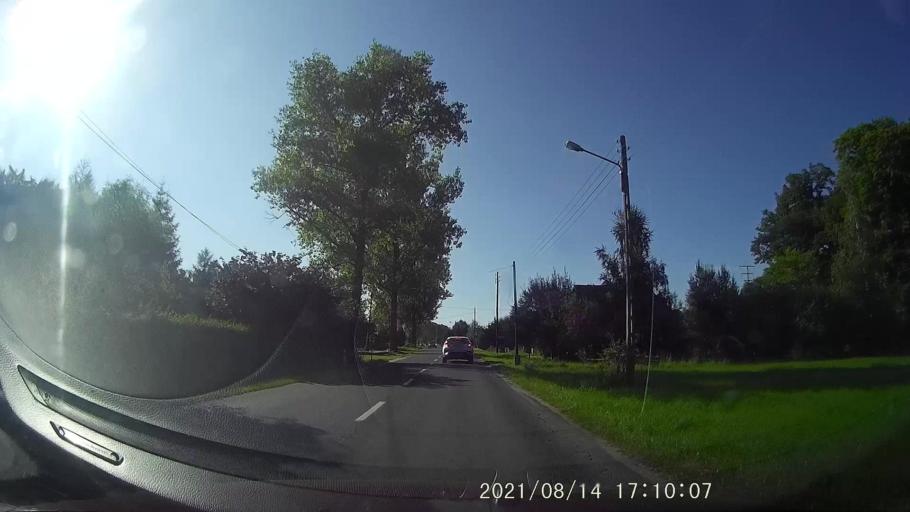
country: PL
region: Lower Silesian Voivodeship
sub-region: Powiat jeleniogorski
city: Myslakowice
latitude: 50.8261
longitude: 15.8000
